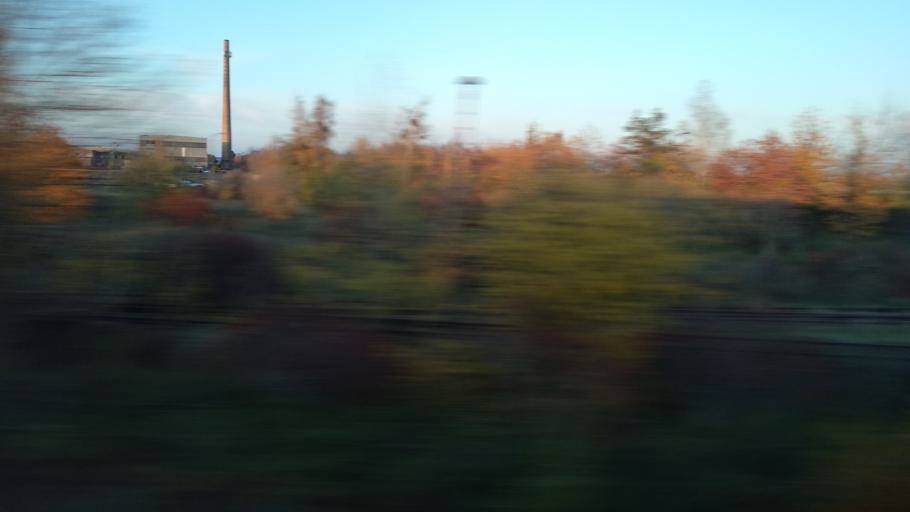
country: DE
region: Saxony
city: Dahlen
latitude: 51.3477
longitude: 12.9967
